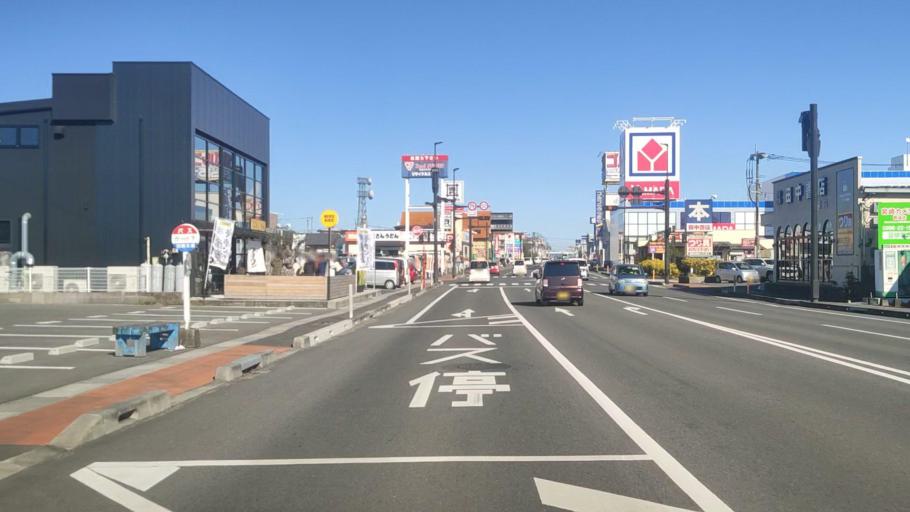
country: JP
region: Miyazaki
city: Miyakonojo
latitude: 31.7381
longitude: 131.0699
